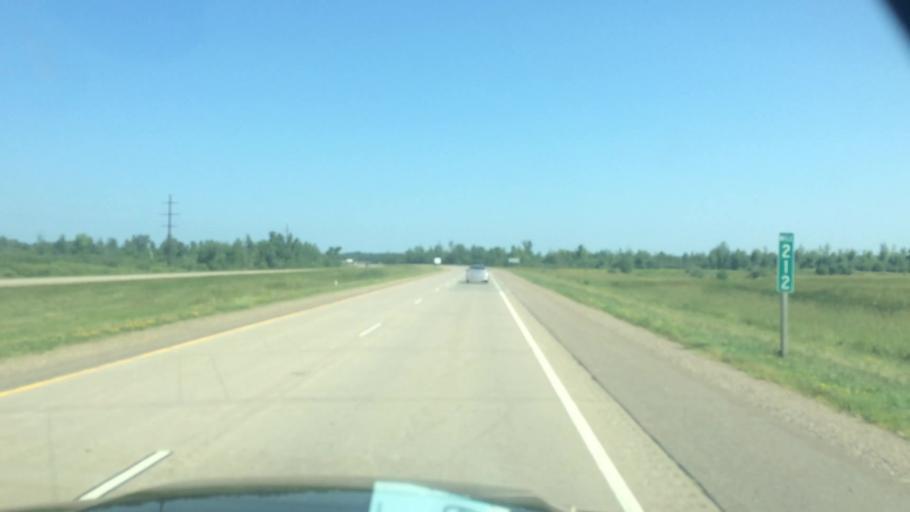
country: US
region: Wisconsin
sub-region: Lincoln County
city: Merrill
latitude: 45.2243
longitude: -89.6708
